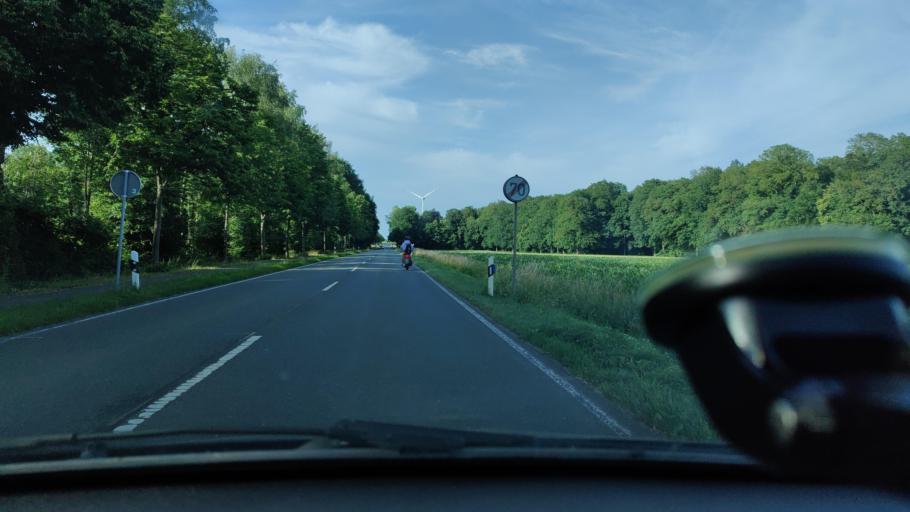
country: DE
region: North Rhine-Westphalia
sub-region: Regierungsbezirk Munster
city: Coesfeld
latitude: 51.9845
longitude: 7.1942
